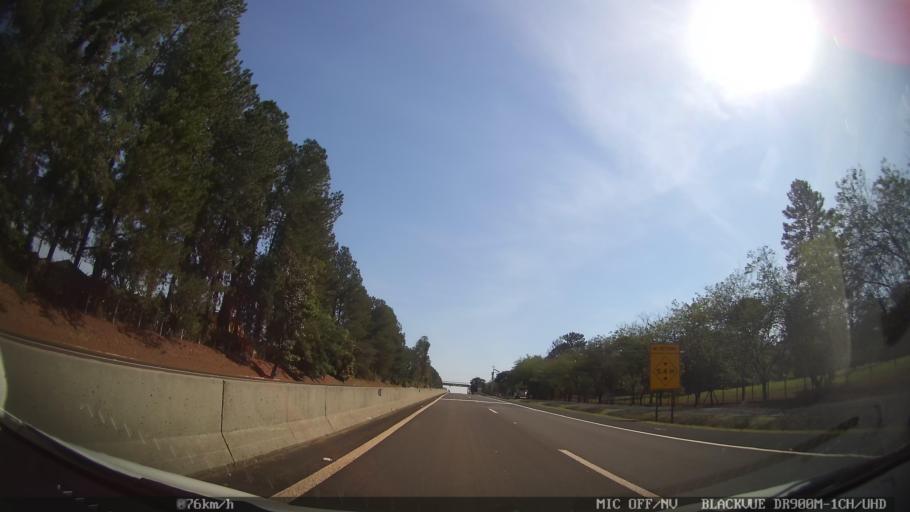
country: BR
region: Sao Paulo
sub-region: Ribeirao Preto
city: Ribeirao Preto
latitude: -21.1743
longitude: -47.8576
